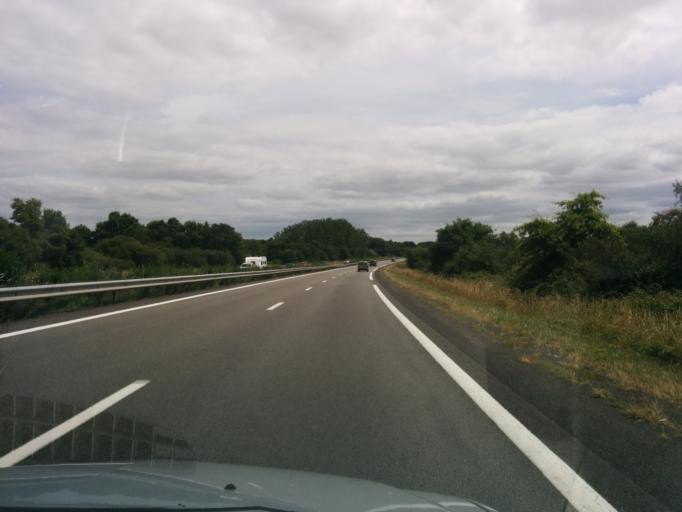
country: FR
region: Pays de la Loire
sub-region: Departement de la Loire-Atlantique
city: La Haie-Fouassiere
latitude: 47.1696
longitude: -1.3781
